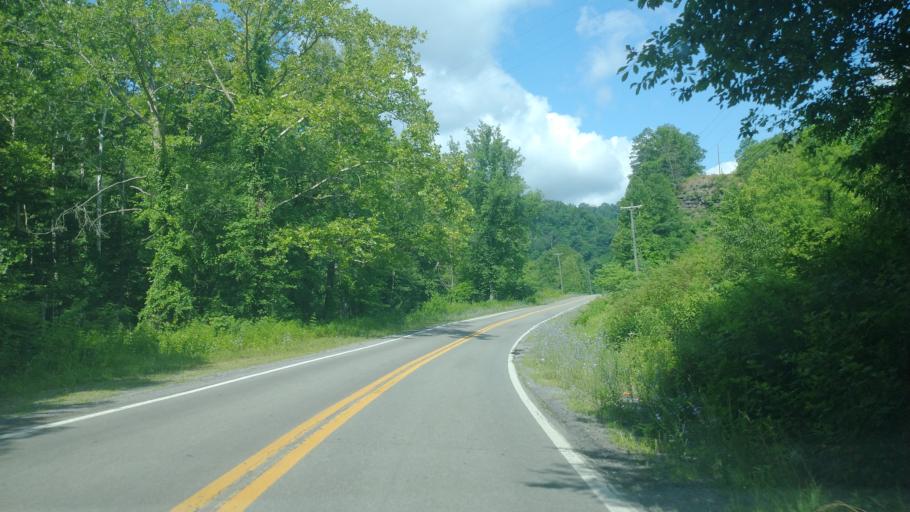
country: US
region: West Virginia
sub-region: McDowell County
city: Welch
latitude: 37.4091
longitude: -81.5328
